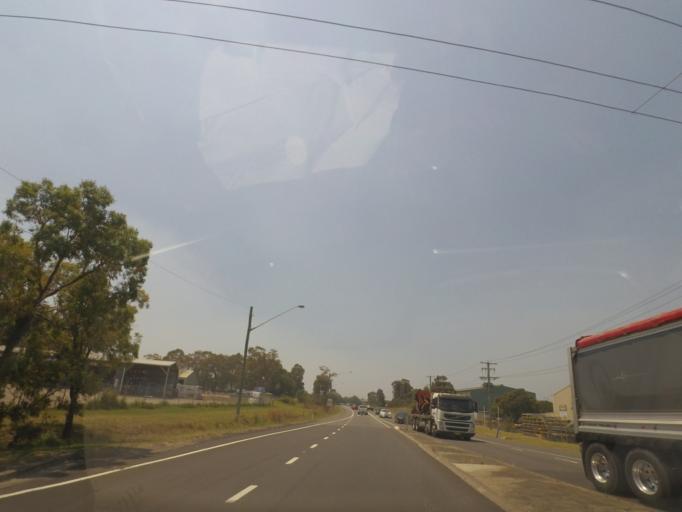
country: AU
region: New South Wales
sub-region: Newcastle
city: Beresfield
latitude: -32.8221
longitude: 151.7012
